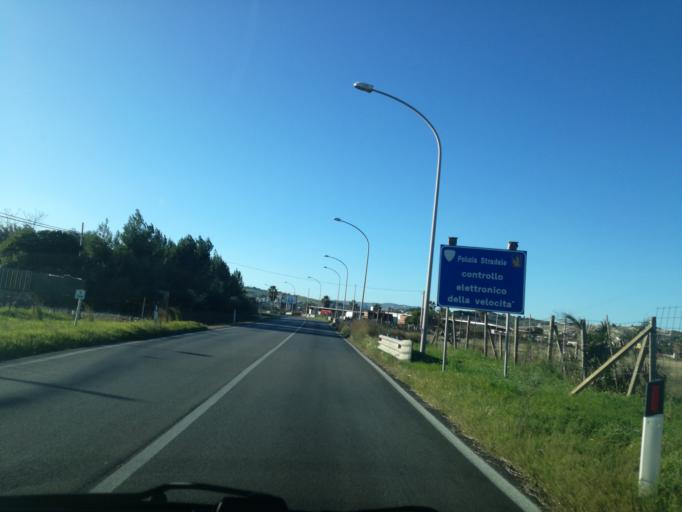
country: IT
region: Sicily
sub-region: Provincia di Caltanissetta
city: Gela
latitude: 37.0960
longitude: 14.1714
